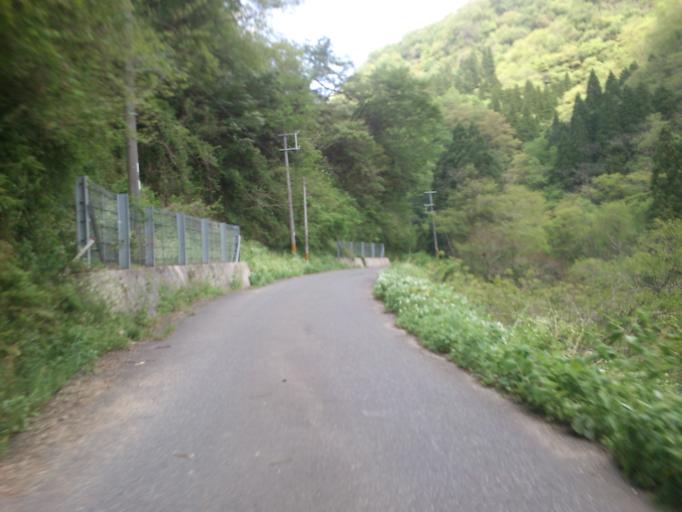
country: JP
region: Kyoto
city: Miyazu
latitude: 35.6648
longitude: 135.1600
